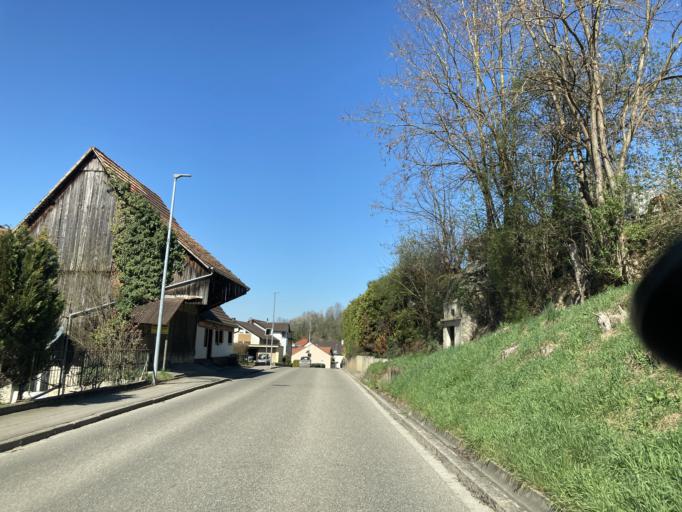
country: DE
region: Baden-Wuerttemberg
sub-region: Freiburg Region
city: Schliengen
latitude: 47.7520
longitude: 7.5862
